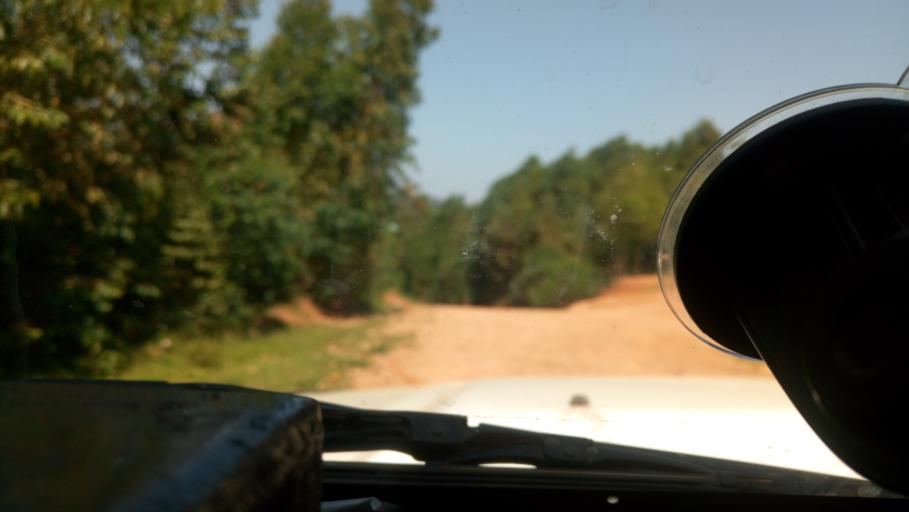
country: KE
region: Kisii
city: Ogembo
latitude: -0.7284
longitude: 34.7079
